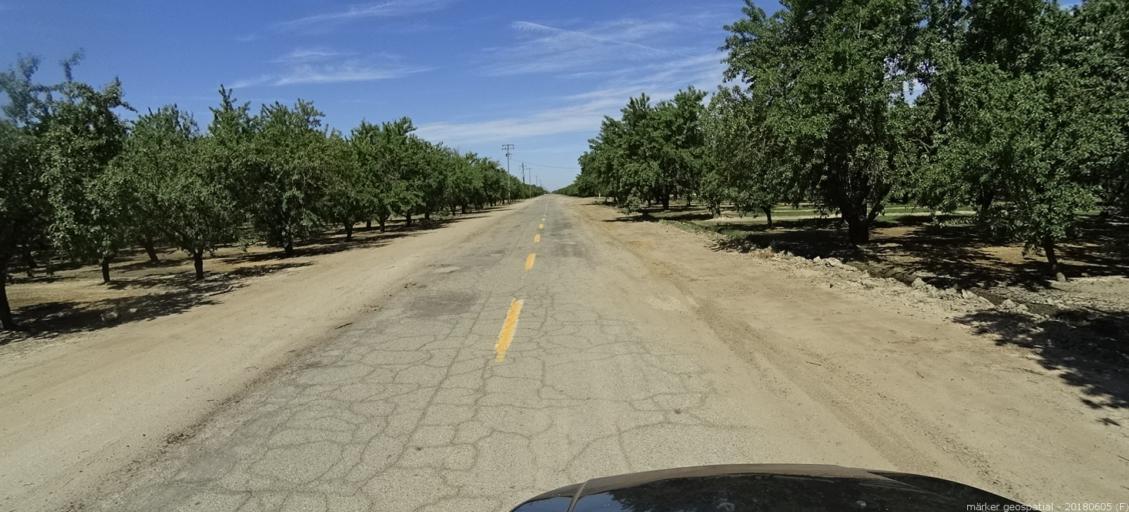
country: US
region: California
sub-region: Madera County
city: Chowchilla
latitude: 37.0982
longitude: -120.3949
